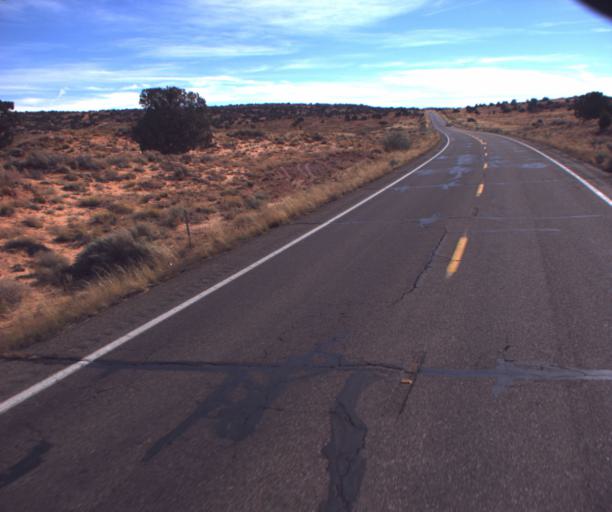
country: US
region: Arizona
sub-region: Coconino County
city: Kaibito
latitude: 36.5812
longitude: -111.1436
